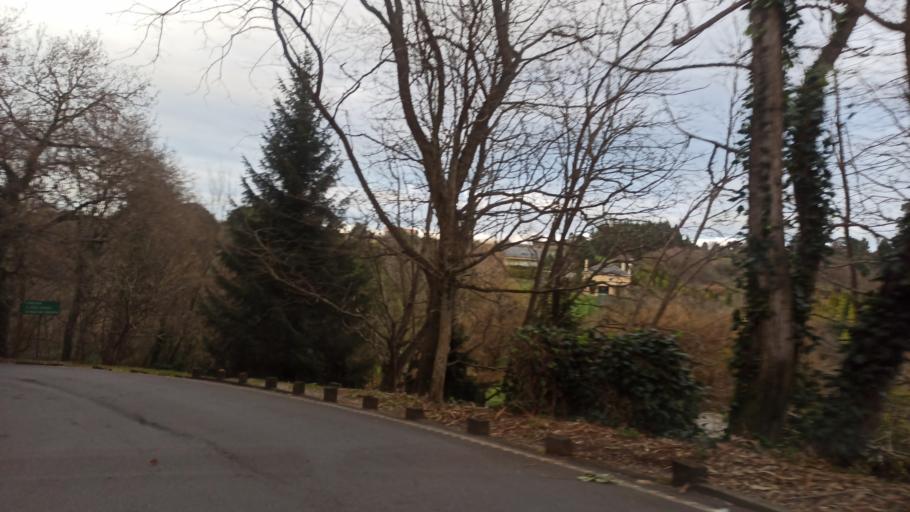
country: ES
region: Galicia
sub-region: Provincia da Coruna
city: Oleiros
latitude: 43.3343
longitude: -8.3520
